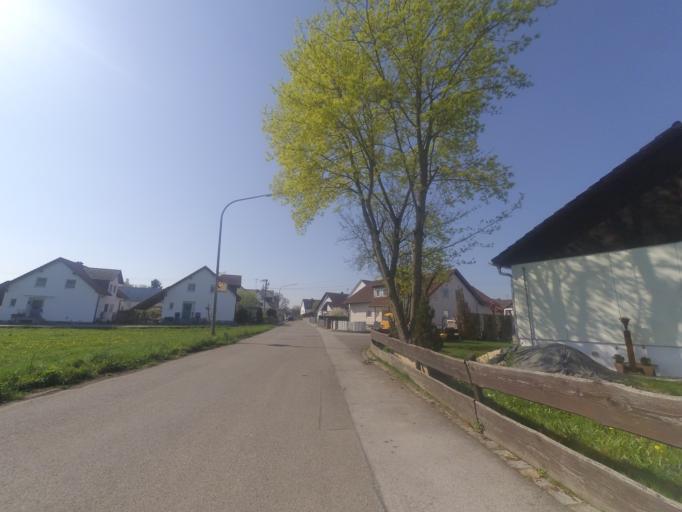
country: DE
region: Bavaria
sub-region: Swabia
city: Nersingen
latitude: 48.4191
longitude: 10.1352
